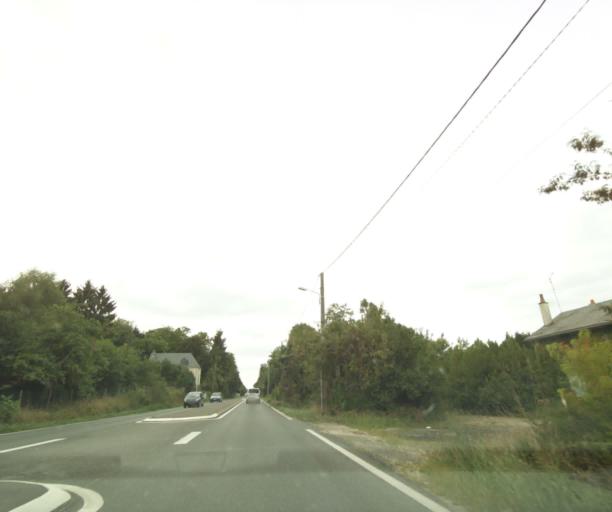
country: FR
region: Centre
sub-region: Departement d'Indre-et-Loire
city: Perrusson
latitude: 47.0768
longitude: 1.0570
